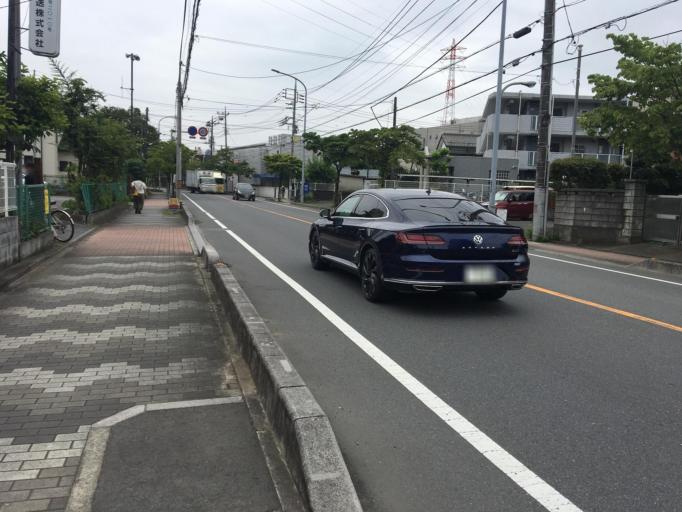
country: JP
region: Saitama
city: Shimotoda
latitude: 35.8038
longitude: 139.6814
